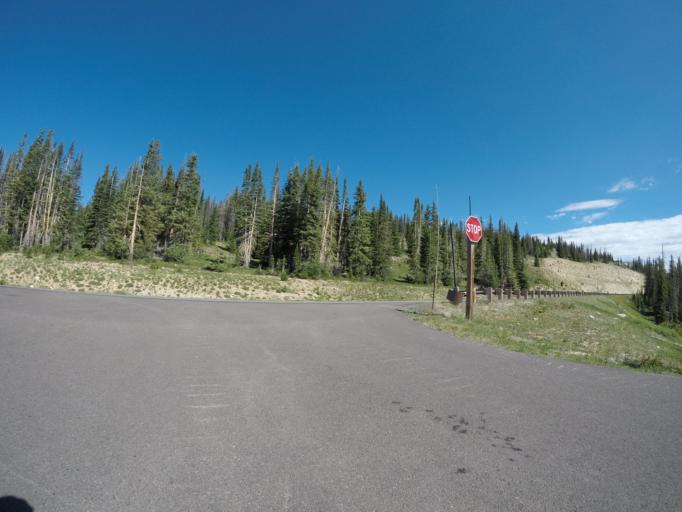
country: US
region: Wyoming
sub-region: Carbon County
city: Saratoga
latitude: 41.3145
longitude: -106.3501
